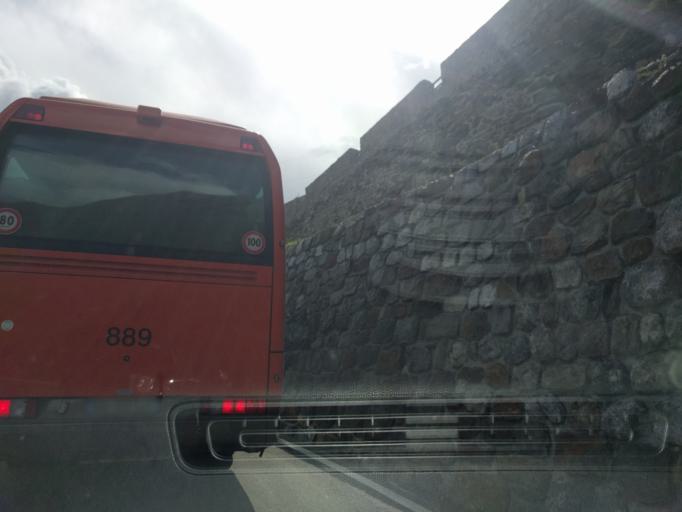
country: IT
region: Lombardy
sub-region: Provincia di Sondrio
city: Sant'Antonio
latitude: 46.5299
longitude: 10.4556
